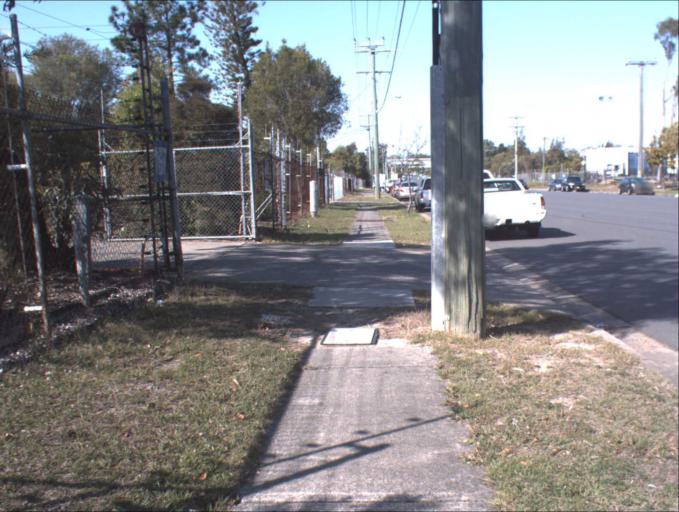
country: AU
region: Queensland
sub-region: Logan
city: Logan Reserve
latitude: -27.6817
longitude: 153.0784
